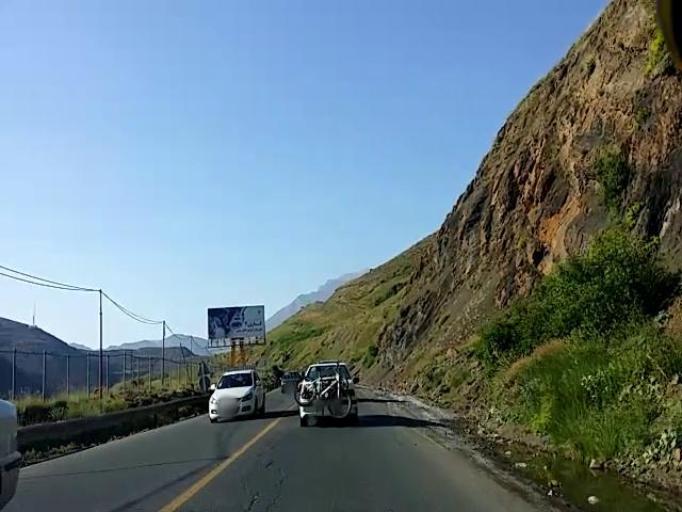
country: IR
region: Tehran
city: Tajrish
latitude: 36.1863
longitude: 51.3198
